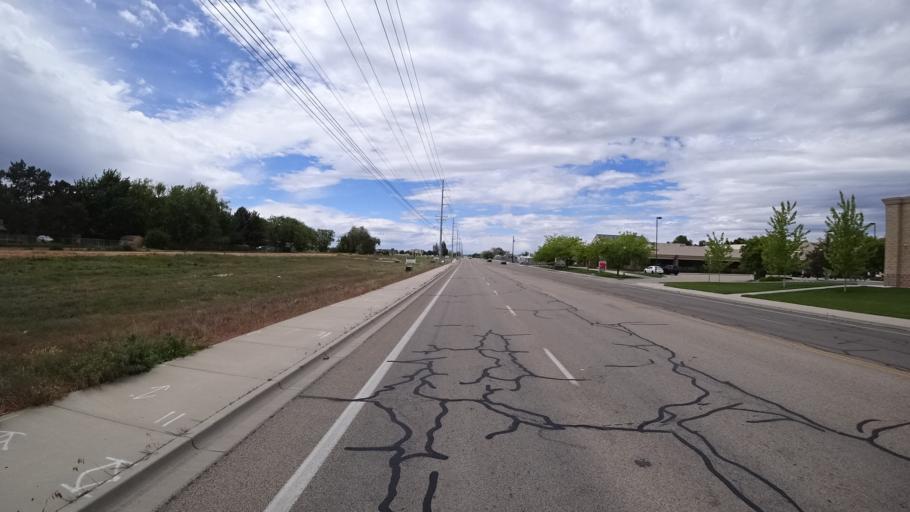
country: US
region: Idaho
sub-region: Ada County
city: Meridian
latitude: 43.5903
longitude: -116.3357
